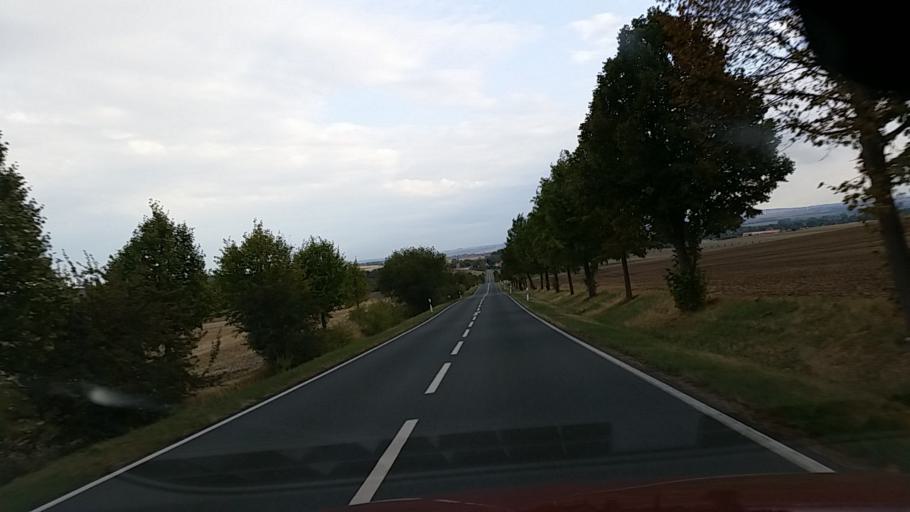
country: DE
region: Thuringia
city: Beichlingen
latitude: 51.2175
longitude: 11.2538
